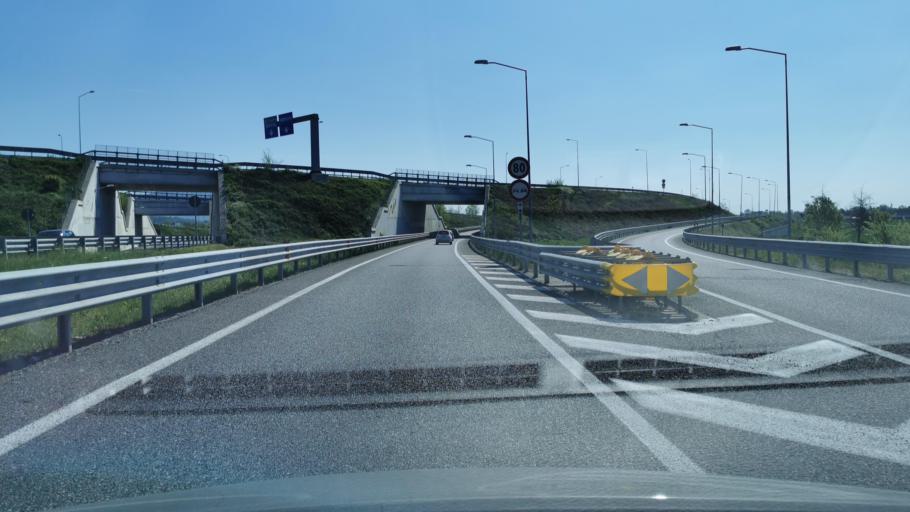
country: IT
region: Lombardy
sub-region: Provincia di Brescia
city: Castegnato
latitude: 45.5477
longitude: 10.1313
